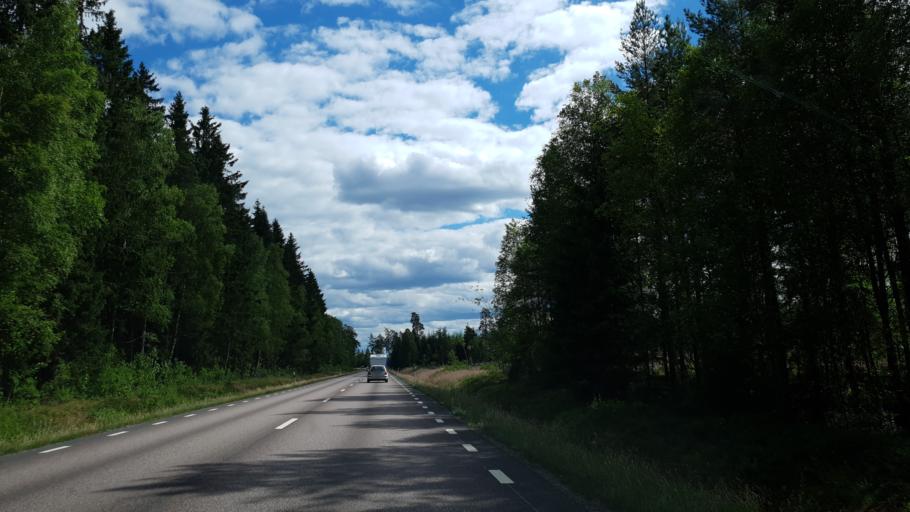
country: SE
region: Kronoberg
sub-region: Lessebo Kommun
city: Lessebo
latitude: 56.8384
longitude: 15.3917
